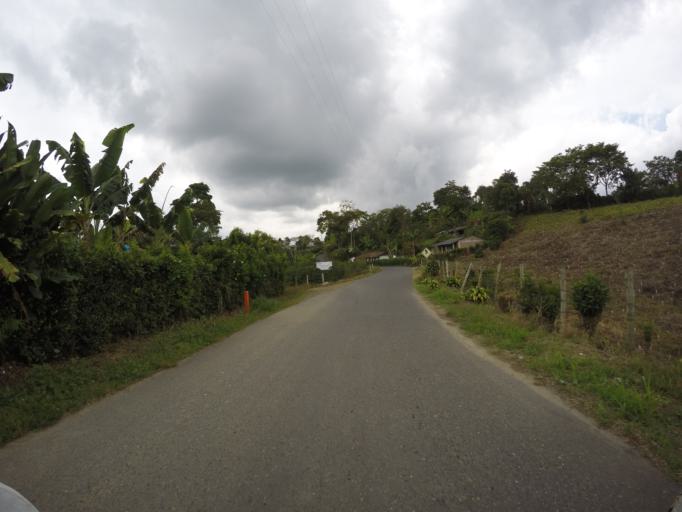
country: CO
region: Quindio
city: Quimbaya
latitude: 4.6142
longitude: -75.7081
